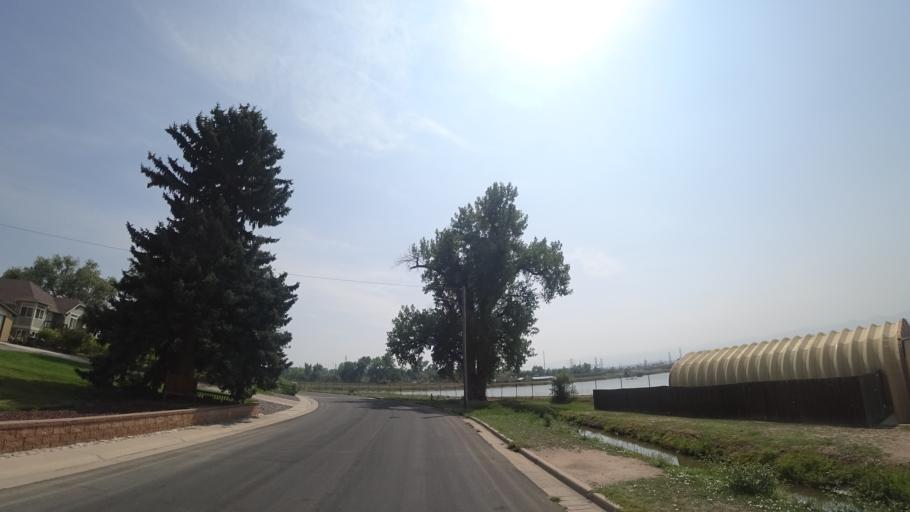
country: US
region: Colorado
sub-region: Arapahoe County
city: Littleton
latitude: 39.6311
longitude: -105.0034
